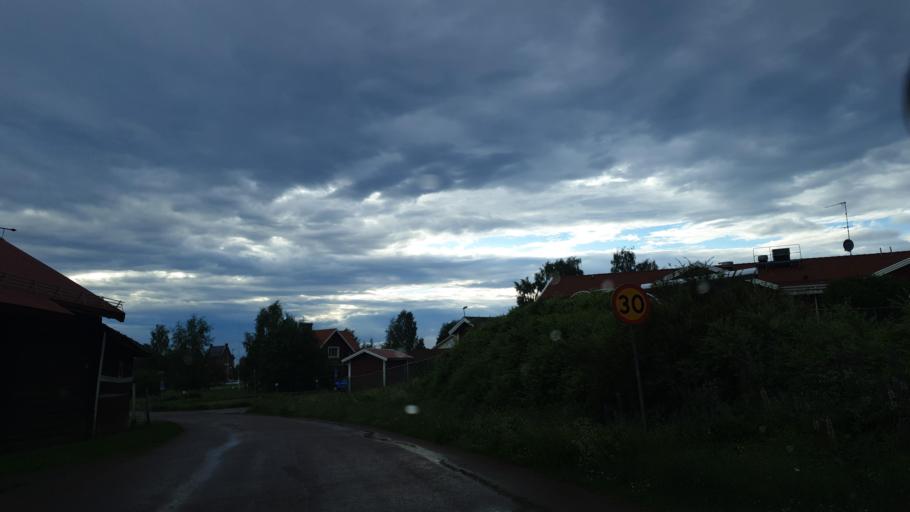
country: SE
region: Dalarna
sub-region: Mora Kommun
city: Mora
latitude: 61.0016
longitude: 14.5839
